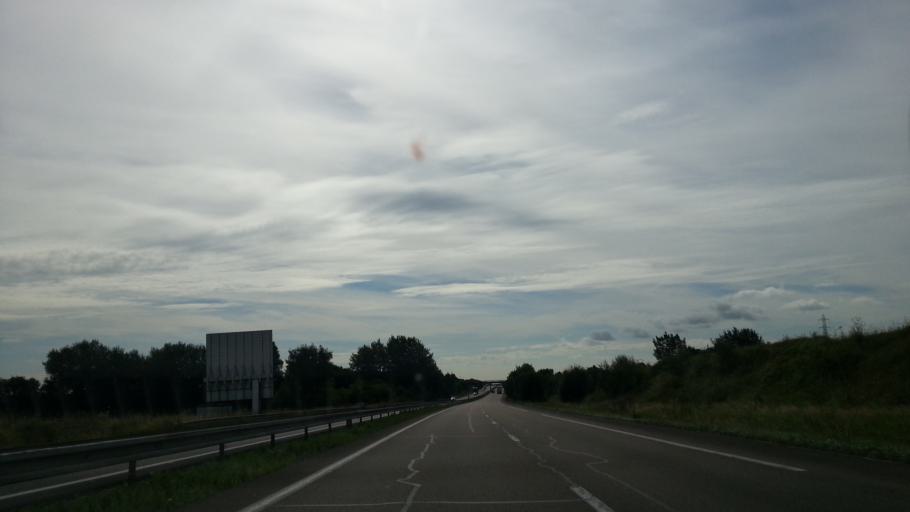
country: FR
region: Champagne-Ardenne
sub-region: Departement de la Marne
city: Sillery
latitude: 49.1985
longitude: 4.1151
